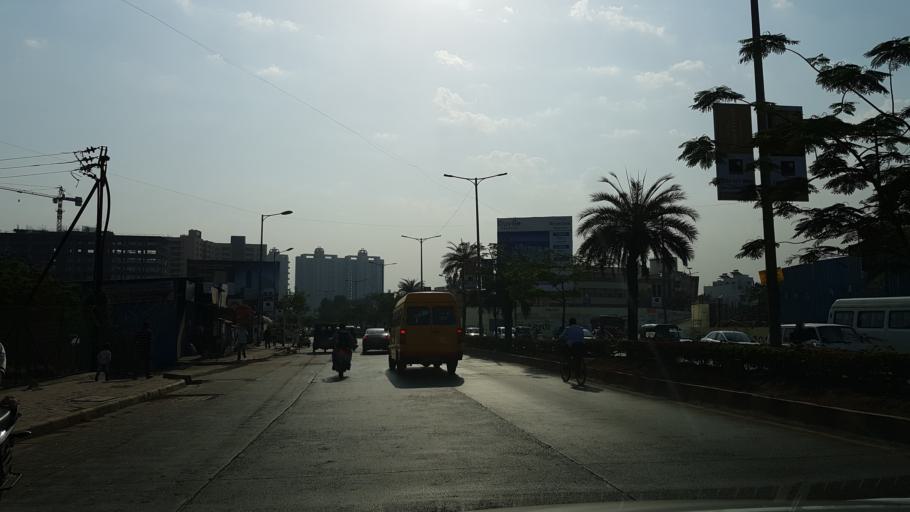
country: IN
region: Maharashtra
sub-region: Pune Division
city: Lohogaon
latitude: 18.5487
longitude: 73.9450
